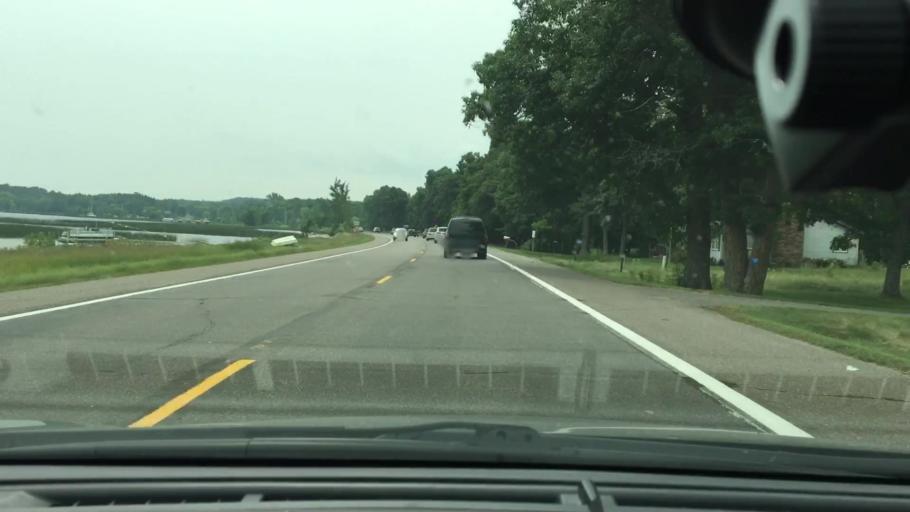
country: US
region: Minnesota
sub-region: Mille Lacs County
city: Vineland
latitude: 46.2582
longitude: -93.8232
